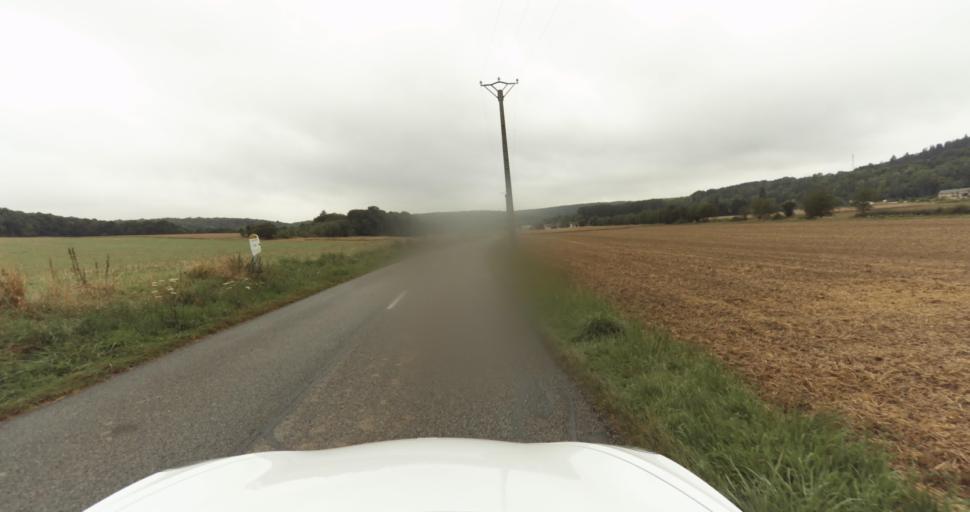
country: FR
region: Haute-Normandie
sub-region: Departement de l'Eure
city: Normanville
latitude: 49.0970
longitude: 1.1305
